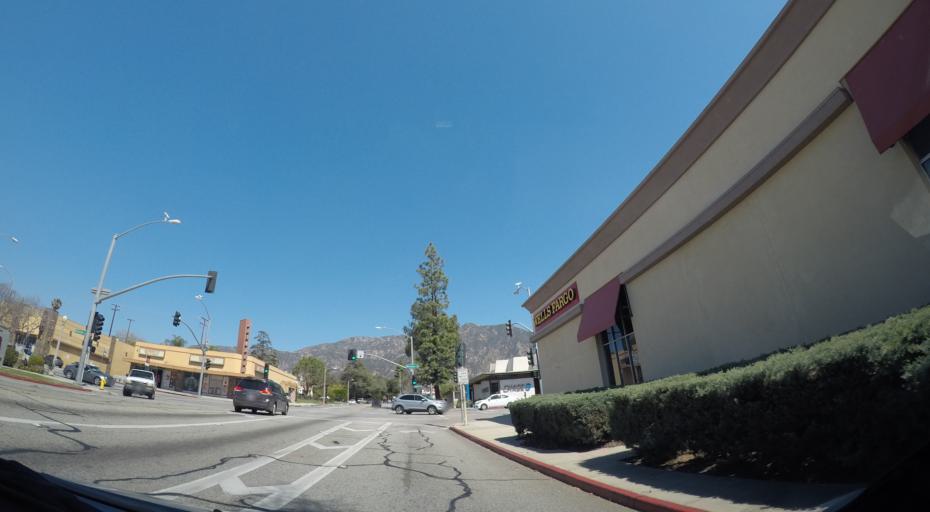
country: US
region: California
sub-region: Los Angeles County
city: Altadena
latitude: 34.1688
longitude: -118.1130
